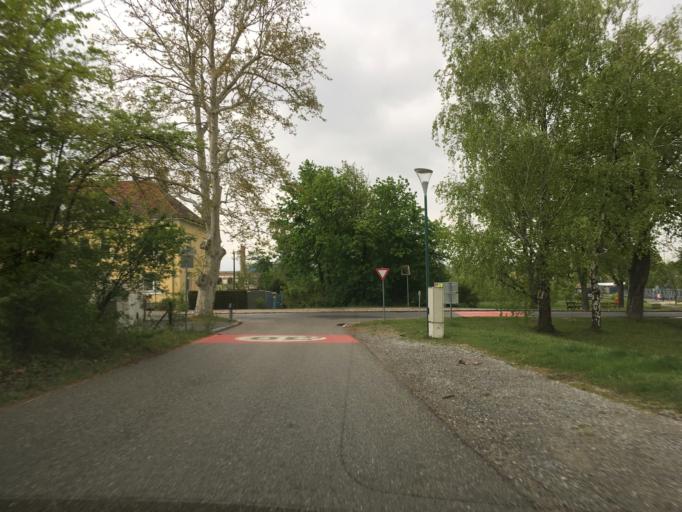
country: AT
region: Burgenland
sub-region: Politischer Bezirk Neusiedl am See
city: Bruckneudorf
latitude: 48.0161
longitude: 16.7788
